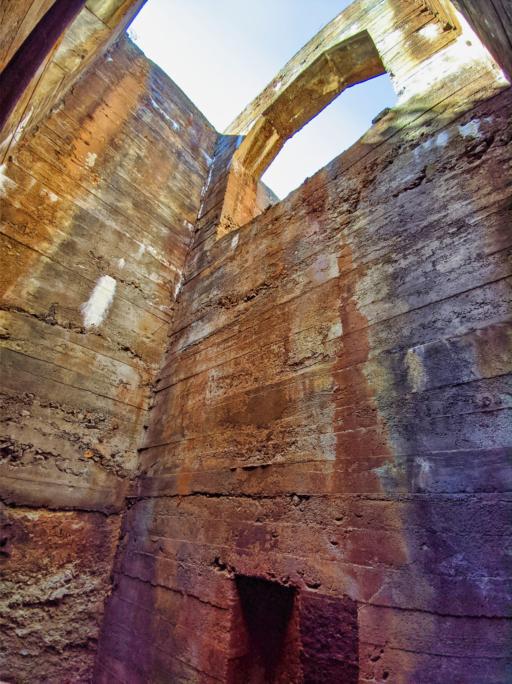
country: NO
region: Sor-Trondelag
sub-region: Meldal
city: Meldal
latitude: 63.1220
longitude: 9.7030
